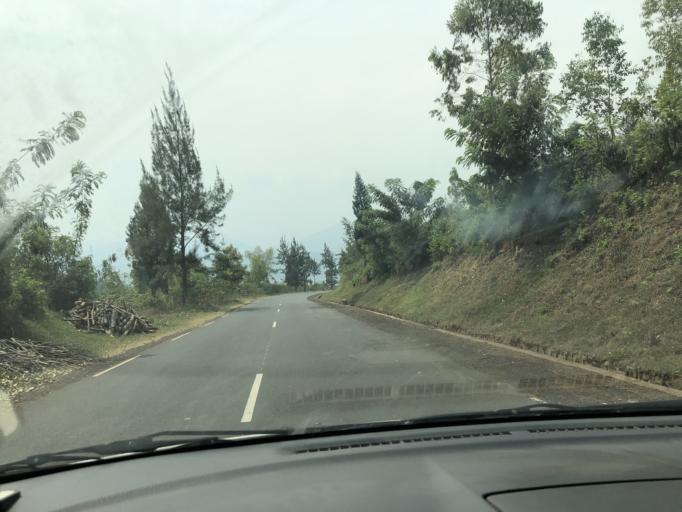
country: RW
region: Western Province
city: Cyangugu
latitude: -2.6686
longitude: 28.9970
